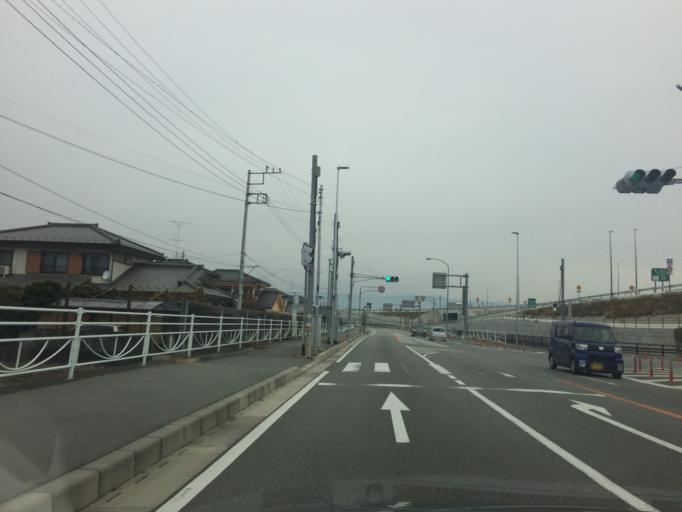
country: JP
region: Yamanashi
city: Ryuo
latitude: 35.5594
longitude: 138.4712
